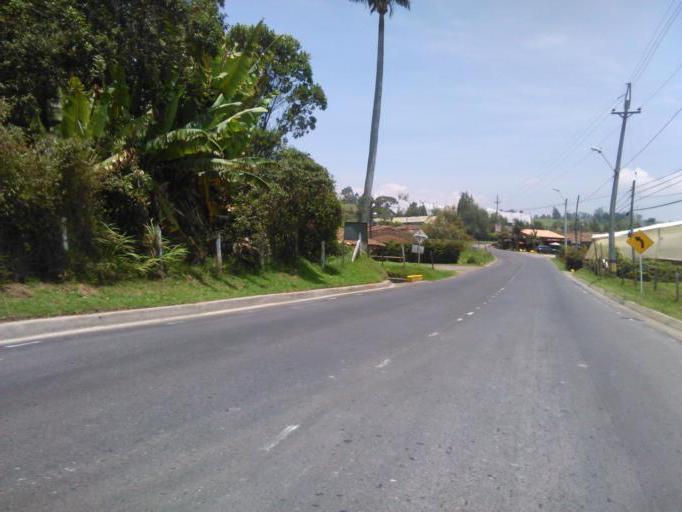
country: CO
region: Antioquia
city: La Union
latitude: 5.9889
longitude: -75.3726
